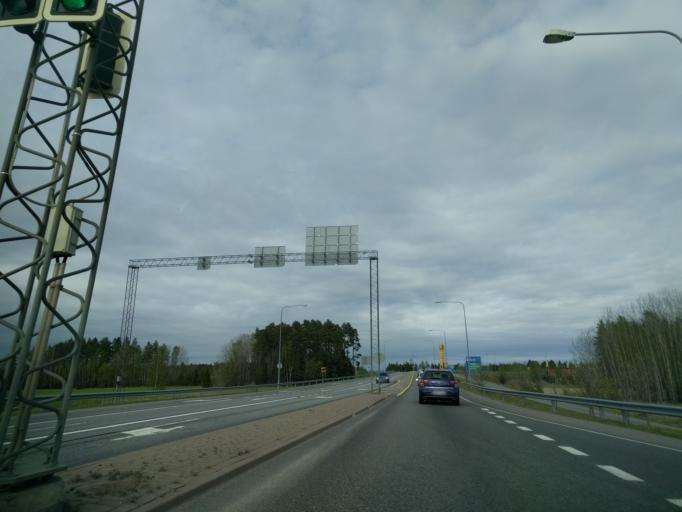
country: FI
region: Varsinais-Suomi
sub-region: Turku
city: Raisio
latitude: 60.5046
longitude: 22.1516
